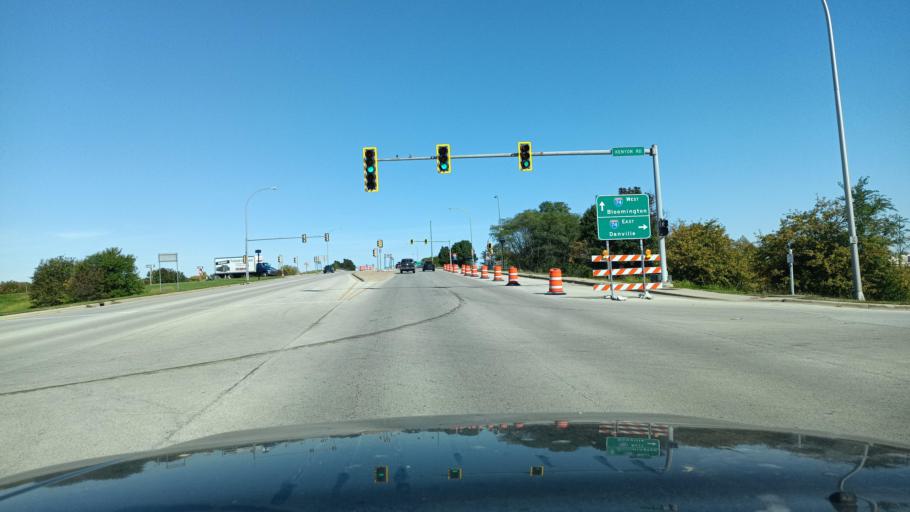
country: US
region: Illinois
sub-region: Champaign County
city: Champaign
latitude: 40.1325
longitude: -88.2436
